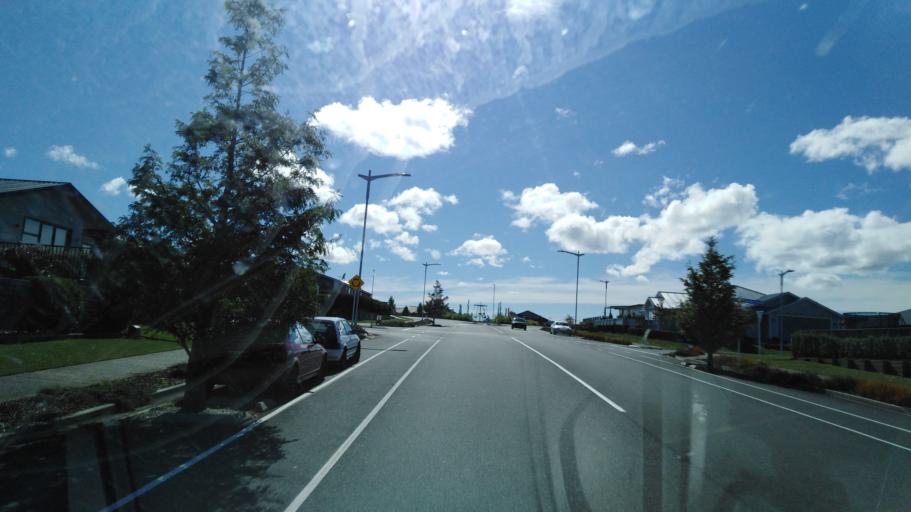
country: NZ
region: Bay of Plenty
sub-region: Tauranga City
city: Tauranga
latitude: -37.7621
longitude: 176.1080
